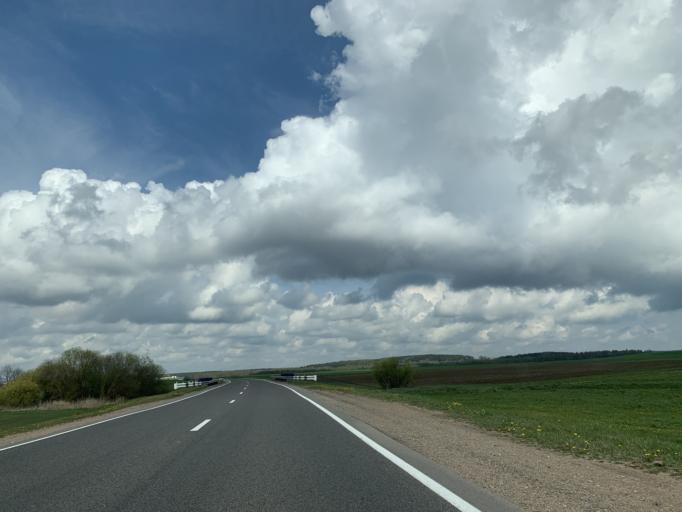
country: BY
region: Minsk
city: Nyasvizh
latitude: 53.2340
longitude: 26.7200
